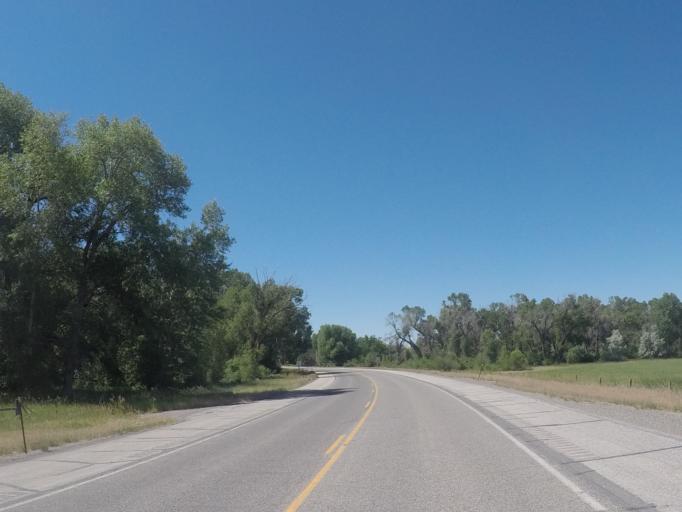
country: US
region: Wyoming
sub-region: Big Horn County
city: Greybull
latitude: 44.5399
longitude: -107.7789
